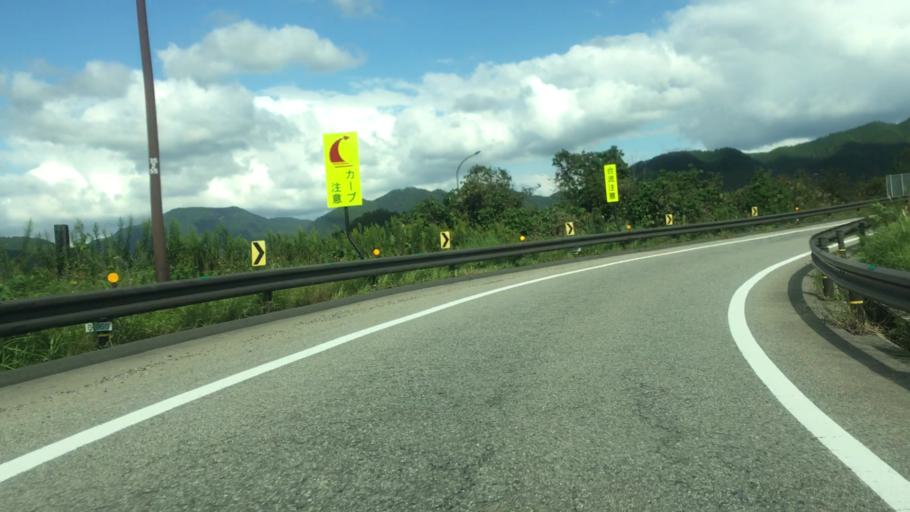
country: JP
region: Hyogo
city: Toyooka
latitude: 35.3129
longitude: 134.8426
